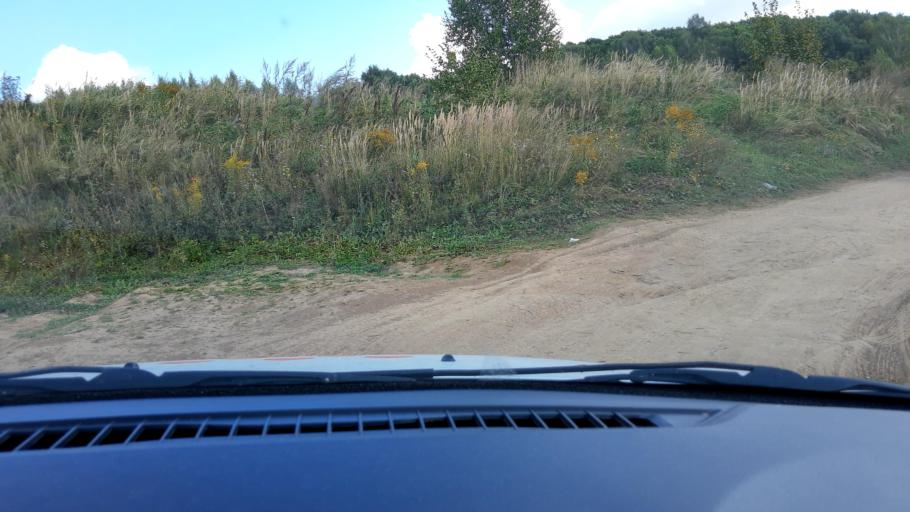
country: RU
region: Nizjnij Novgorod
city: Nizhniy Novgorod
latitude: 56.1988
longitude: 43.9630
